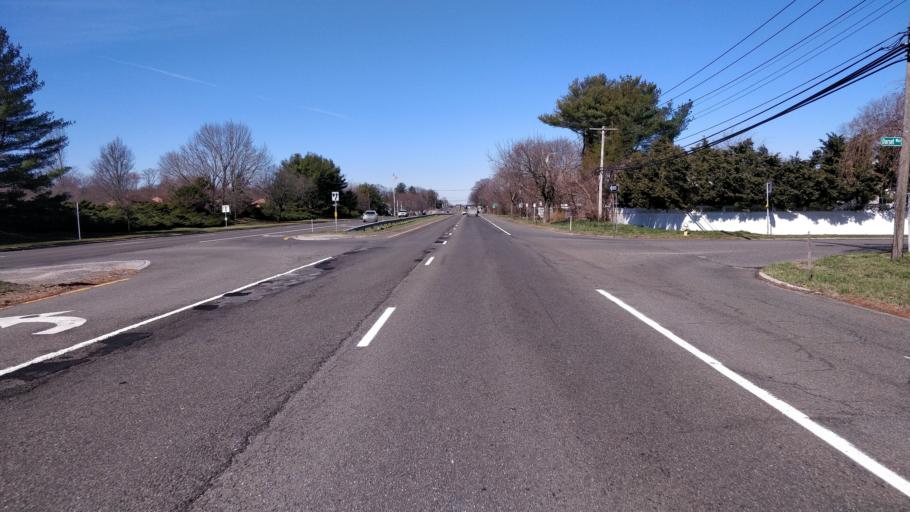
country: US
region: New York
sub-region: Suffolk County
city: Commack
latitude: 40.8371
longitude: -73.2732
